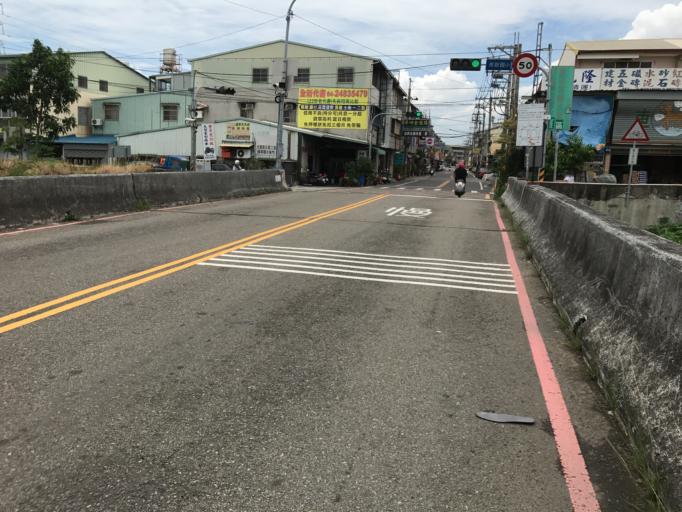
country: TW
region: Taiwan
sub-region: Taichung City
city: Taichung
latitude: 24.0821
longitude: 120.7091
